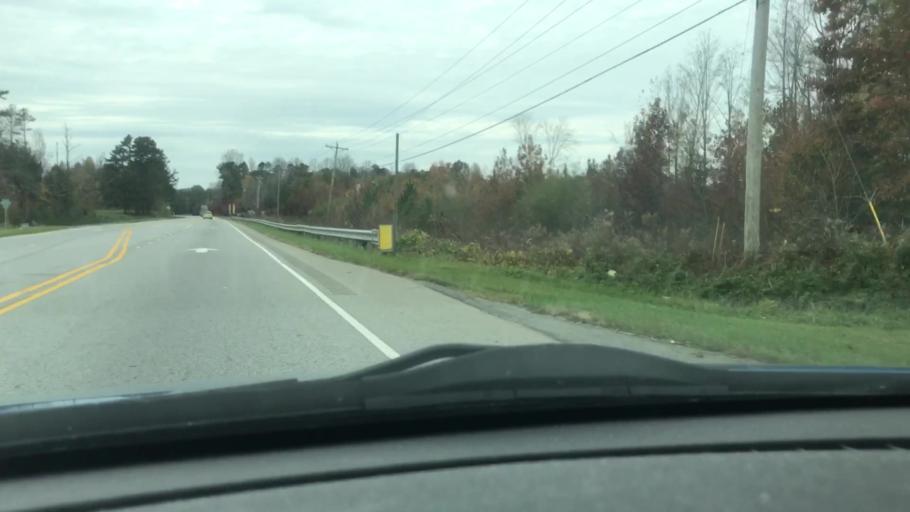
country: US
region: North Carolina
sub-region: Randolph County
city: Trinity
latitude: 35.7478
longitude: -80.0072
